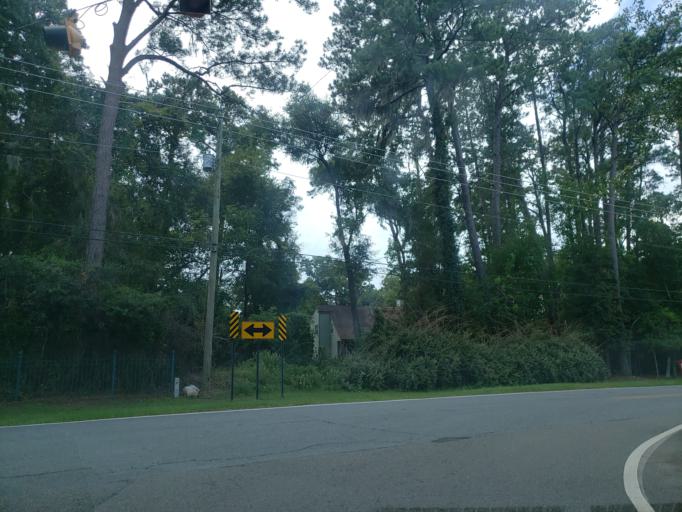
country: US
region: Georgia
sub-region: Chatham County
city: Wilmington Island
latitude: 32.0010
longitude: -80.9690
